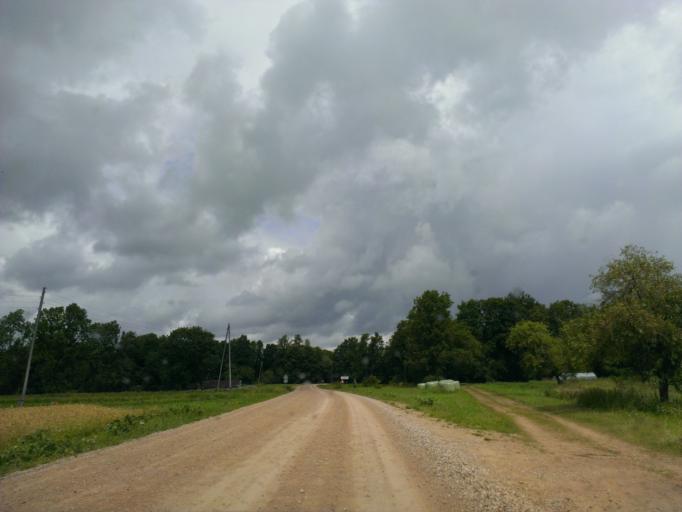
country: LV
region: Sigulda
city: Sigulda
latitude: 57.1973
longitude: 24.9466
